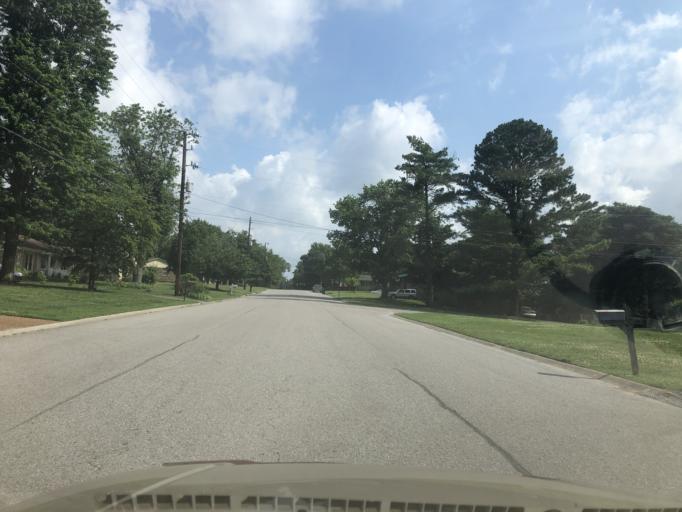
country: US
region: Tennessee
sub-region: Wilson County
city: Green Hill
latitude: 36.2266
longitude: -86.5917
